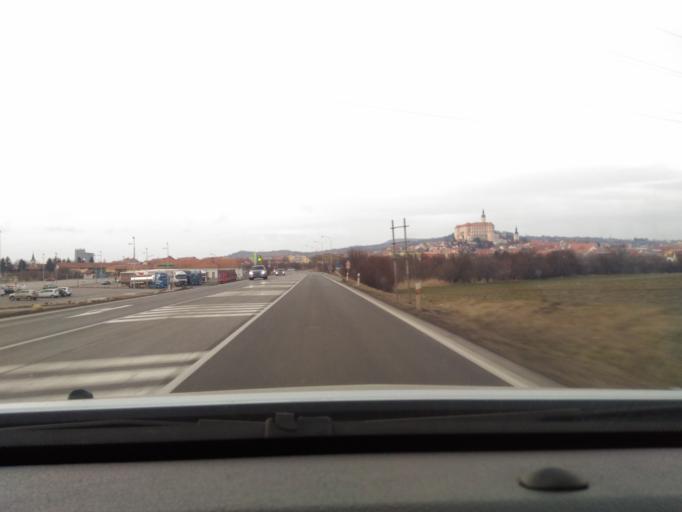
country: CZ
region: South Moravian
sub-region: Okres Breclav
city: Mikulov
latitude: 48.7962
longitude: 16.6332
